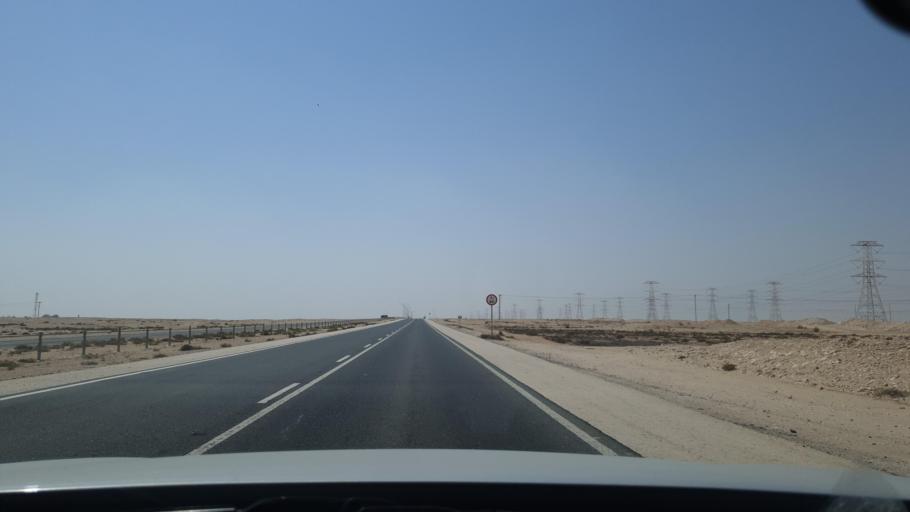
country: QA
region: Al Khawr
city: Al Khawr
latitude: 25.7394
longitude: 51.4605
